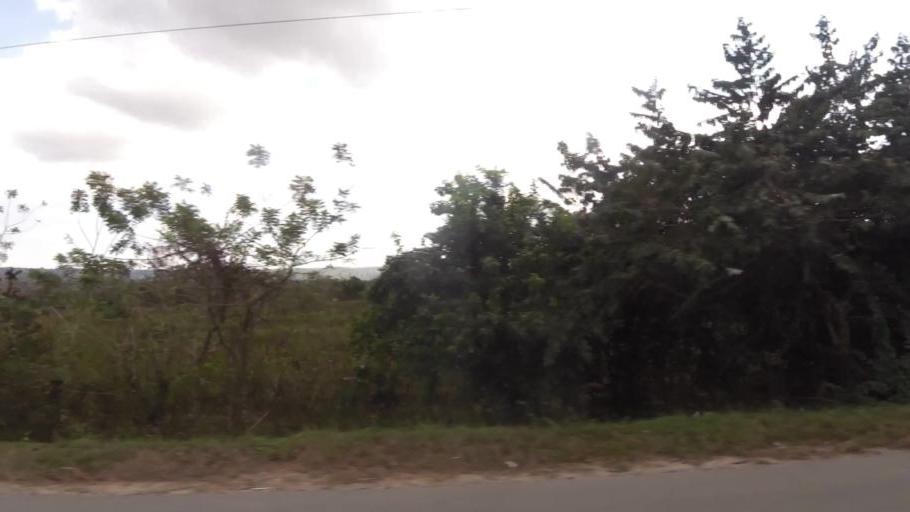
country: CO
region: Bolivar
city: Turbaco
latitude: 10.3635
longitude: -75.4610
